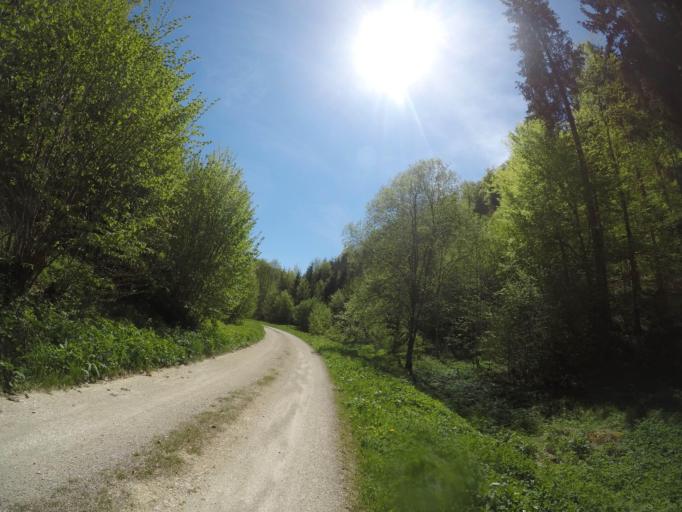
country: DE
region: Baden-Wuerttemberg
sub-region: Tuebingen Region
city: Schelklingen
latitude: 48.4076
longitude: 9.7243
